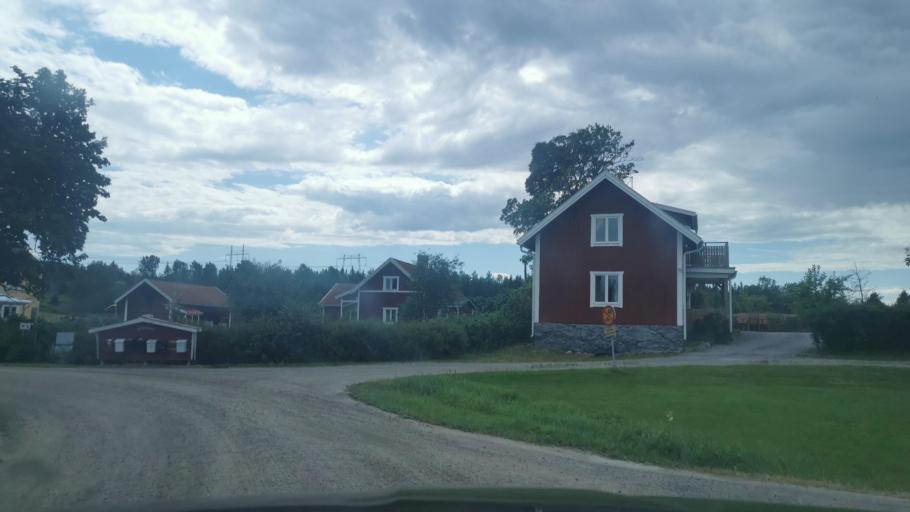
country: SE
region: OEstergoetland
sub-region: Norrkopings Kommun
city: Svartinge
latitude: 58.7169
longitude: 15.9469
